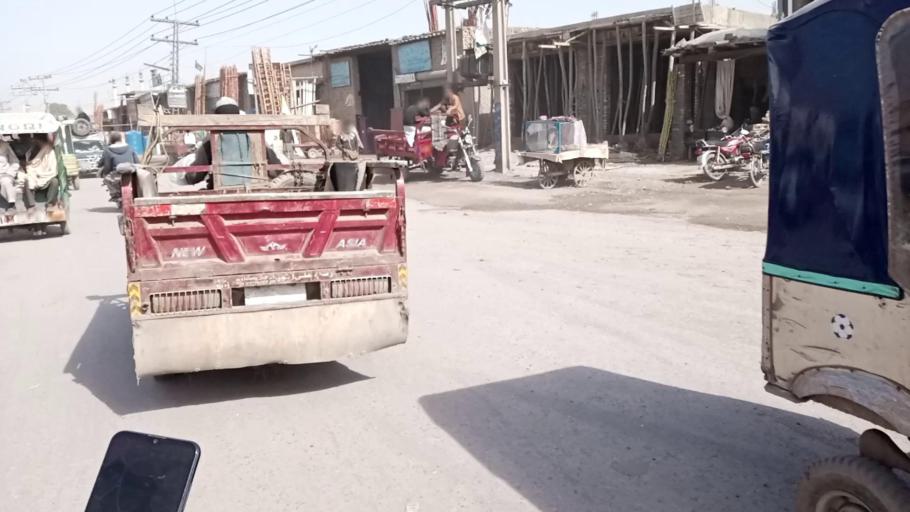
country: PK
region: Khyber Pakhtunkhwa
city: Peshawar
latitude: 33.9845
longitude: 71.6337
